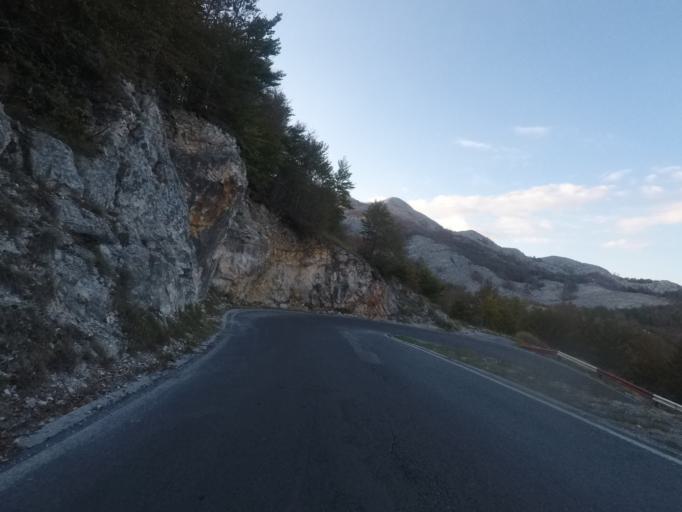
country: ME
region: Cetinje
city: Cetinje
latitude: 42.3843
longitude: 18.8537
